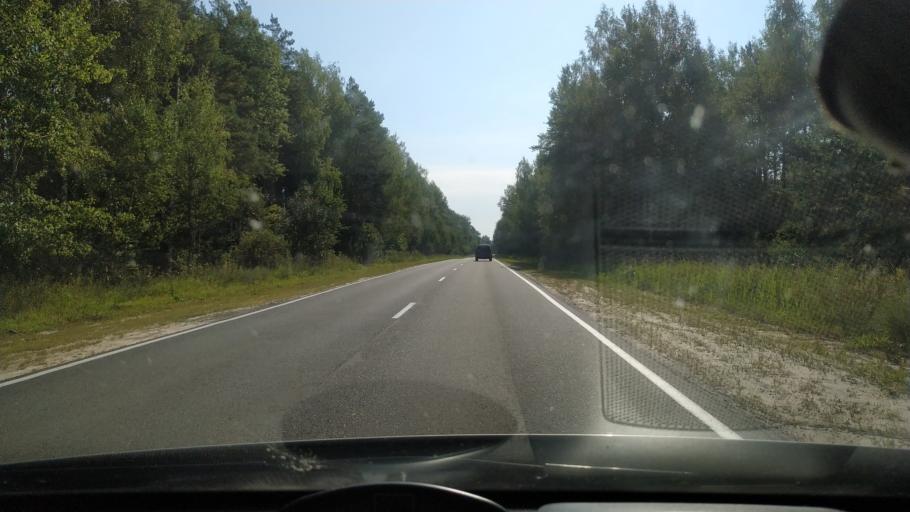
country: RU
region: Rjazan
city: Spas-Klepiki
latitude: 55.2215
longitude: 40.0830
